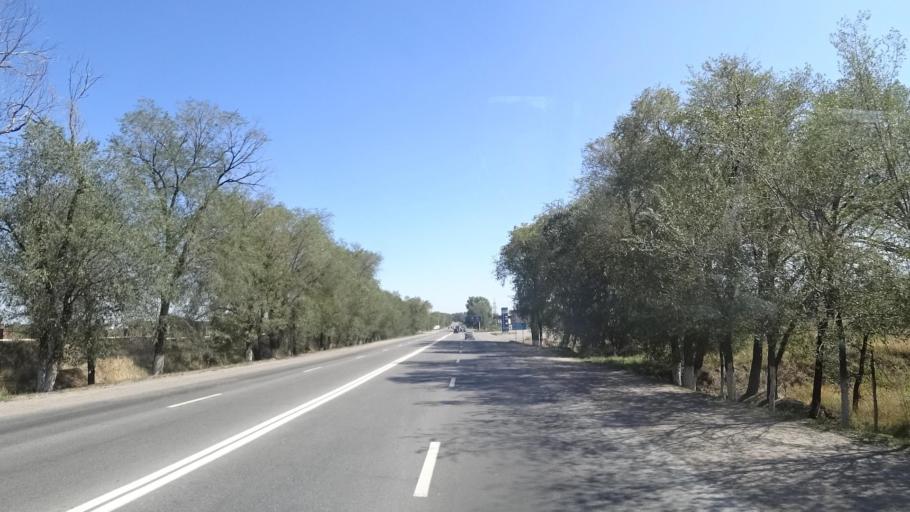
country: KZ
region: Almaty Oblysy
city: Talghar
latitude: 43.3987
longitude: 77.1649
